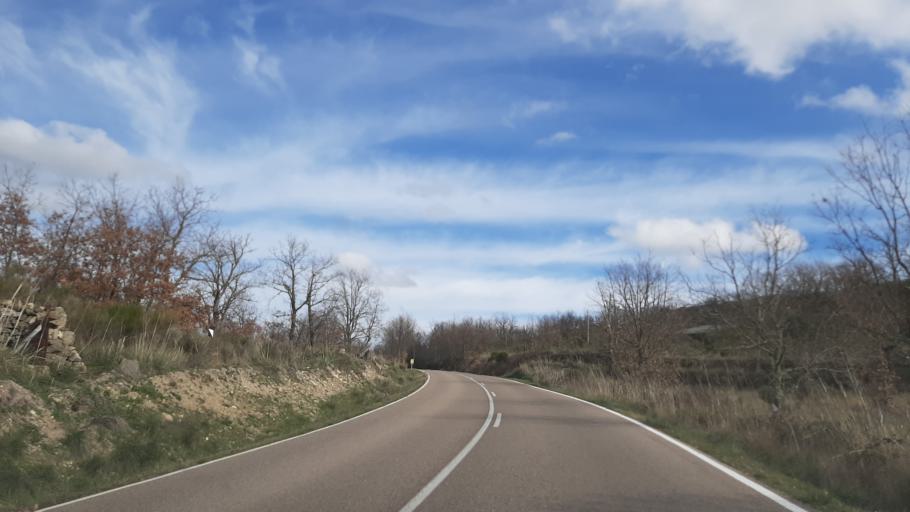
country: ES
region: Castille and Leon
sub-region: Provincia de Salamanca
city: Villarino de los Aires
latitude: 41.2620
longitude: -6.4327
